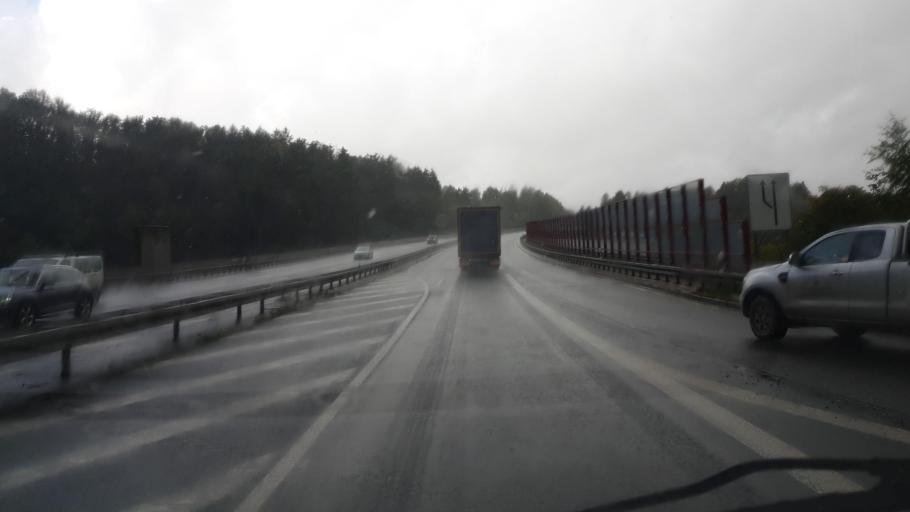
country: DE
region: Saxony
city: Zschopau
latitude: 50.7411
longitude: 13.0642
